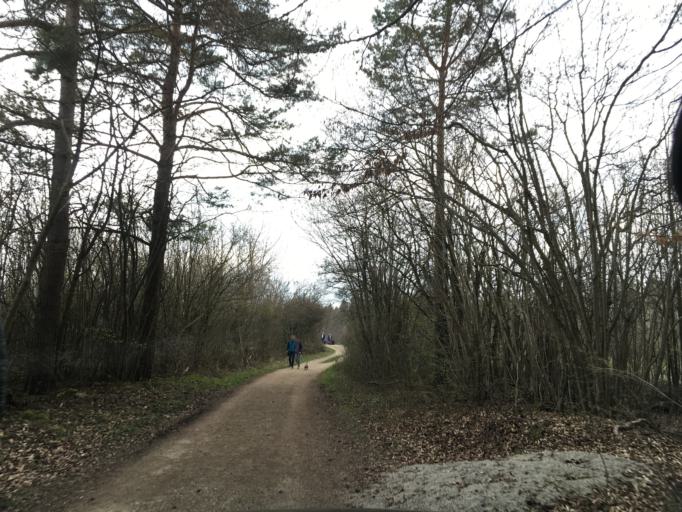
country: DE
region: Bavaria
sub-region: Upper Franconia
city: Pottenstein
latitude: 49.7619
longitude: 11.4296
